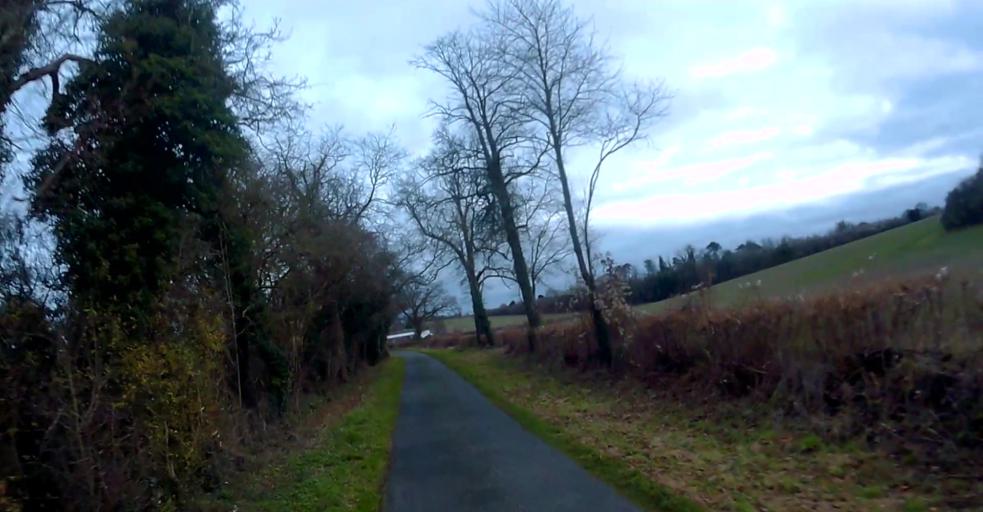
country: GB
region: England
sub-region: Hampshire
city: Overton
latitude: 51.2587
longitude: -1.2342
